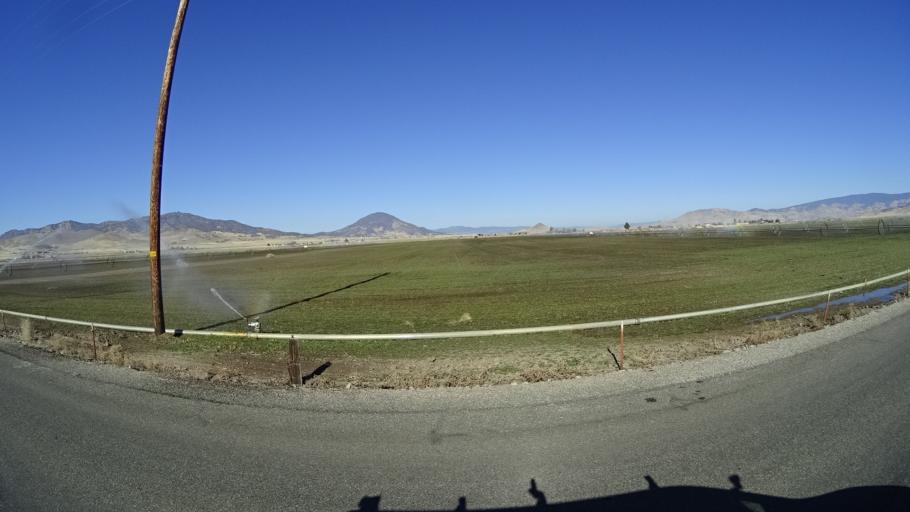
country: US
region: California
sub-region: Siskiyou County
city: Montague
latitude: 41.7561
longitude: -122.4913
